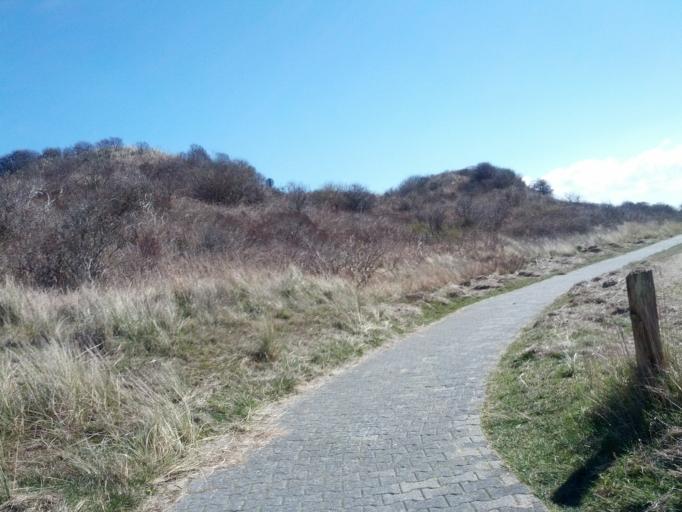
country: DE
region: Lower Saxony
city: Spiekeroog
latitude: 53.7499
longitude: 7.6153
